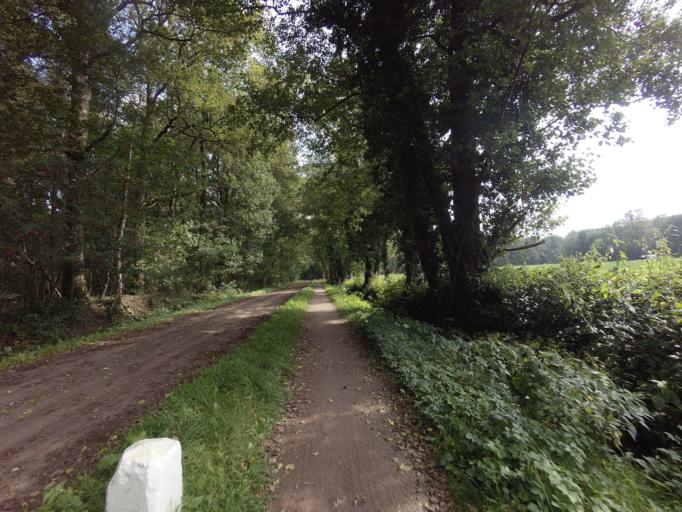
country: NL
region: Overijssel
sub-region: Gemeente Hengelo
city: Hengelo
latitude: 52.2626
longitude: 6.8459
